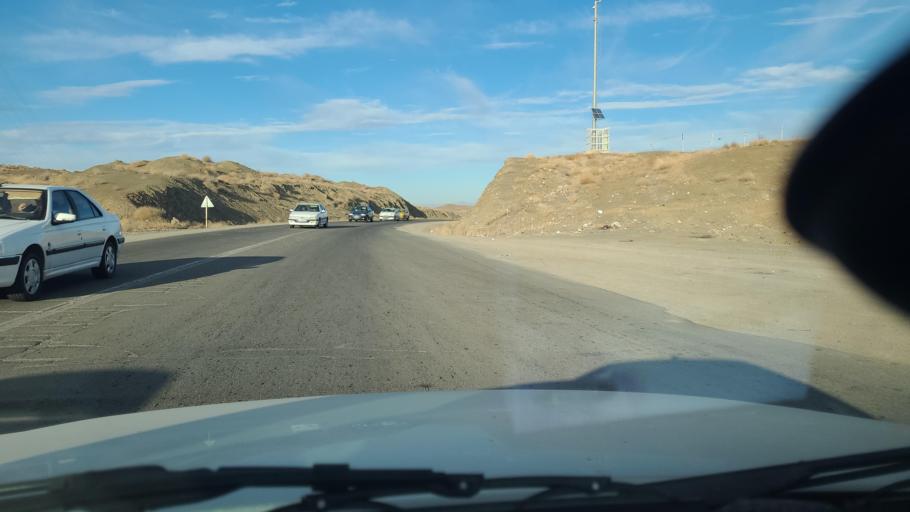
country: IR
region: Razavi Khorasan
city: Sabzevar
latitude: 36.4093
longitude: 57.5487
